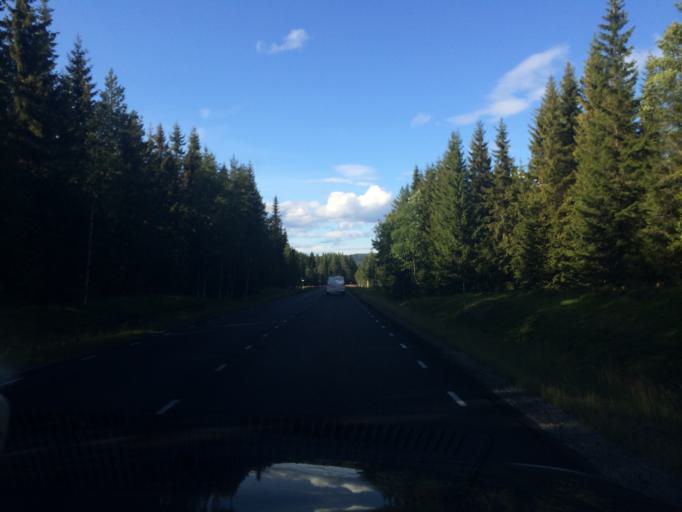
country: NO
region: Hedmark
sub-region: Trysil
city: Innbygda
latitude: 61.0805
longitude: 11.9793
